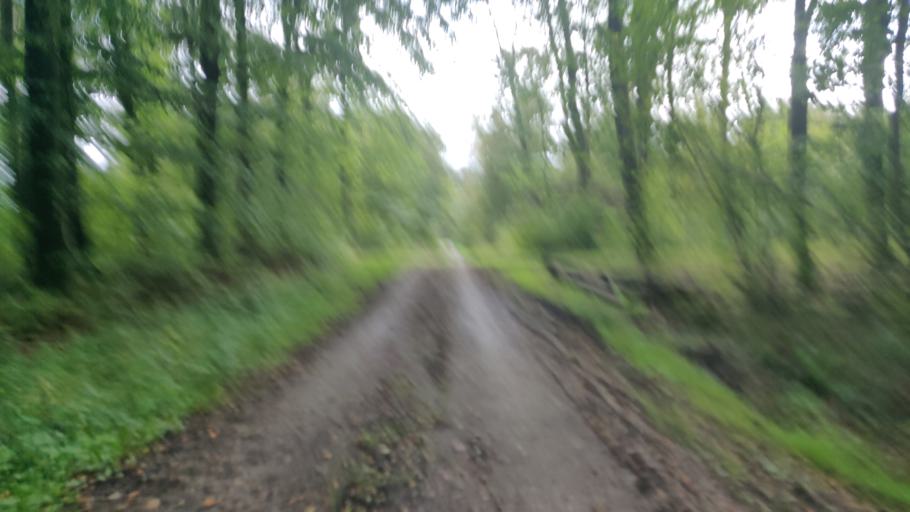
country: DK
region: South Denmark
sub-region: Kolding Kommune
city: Lunderskov
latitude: 55.5437
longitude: 9.3648
